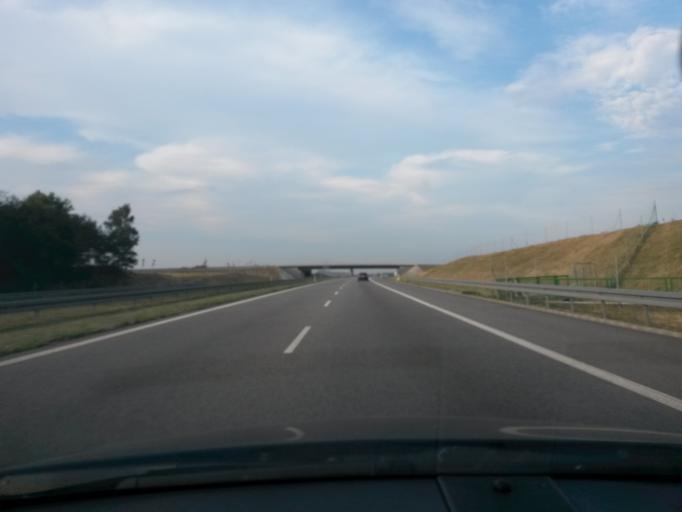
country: PL
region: Lodz Voivodeship
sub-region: powiat Lowicki
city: Lyszkowice
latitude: 51.9631
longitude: 19.8549
